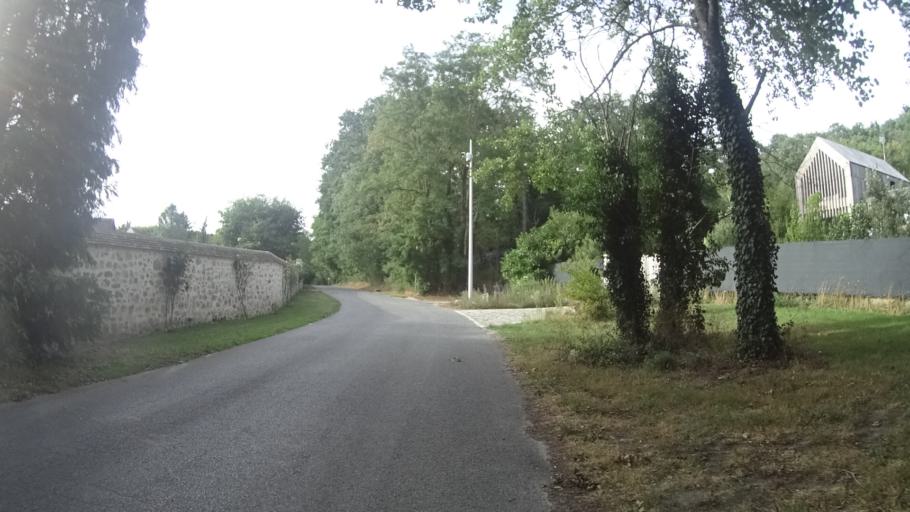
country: FR
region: Picardie
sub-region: Departement de l'Oise
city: Ver-sur-Launette
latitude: 49.1287
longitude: 2.7025
